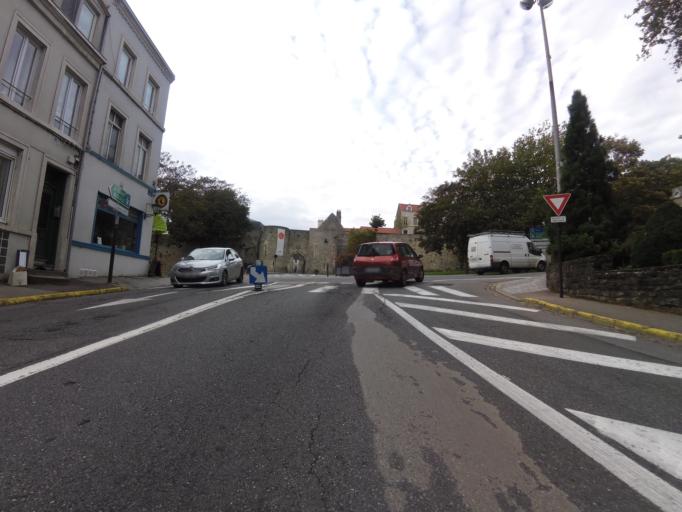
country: FR
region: Nord-Pas-de-Calais
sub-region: Departement du Pas-de-Calais
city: Saint-Martin-Boulogne
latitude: 50.7232
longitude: 1.6159
